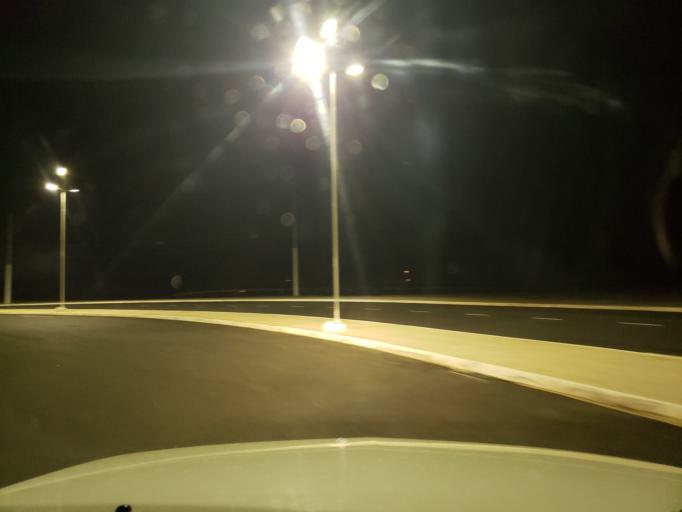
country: BR
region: Sao Paulo
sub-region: Mogi-Mirim
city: Mogi Mirim
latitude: -22.4005
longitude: -46.9724
